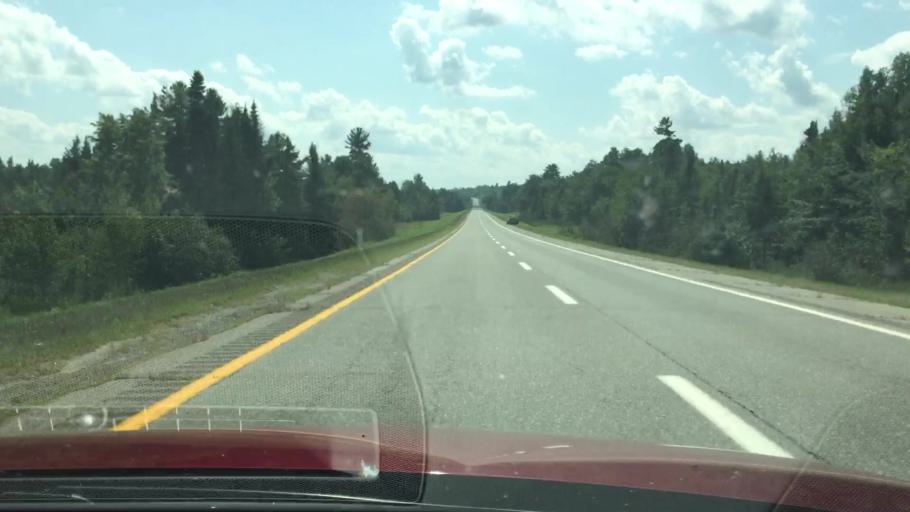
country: US
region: Maine
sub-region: Penobscot County
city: Lincoln
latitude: 45.4768
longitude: -68.5768
